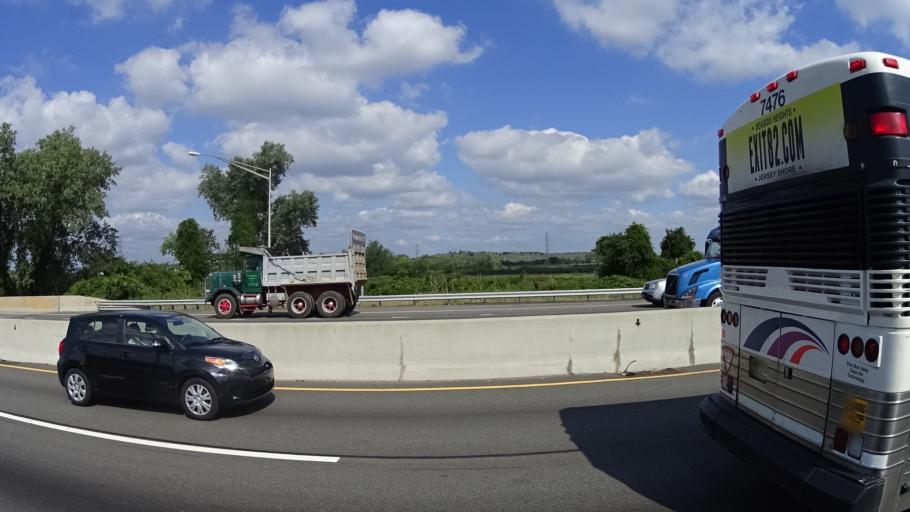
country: US
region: New Jersey
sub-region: Hudson County
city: Kearny
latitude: 40.7545
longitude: -74.1084
